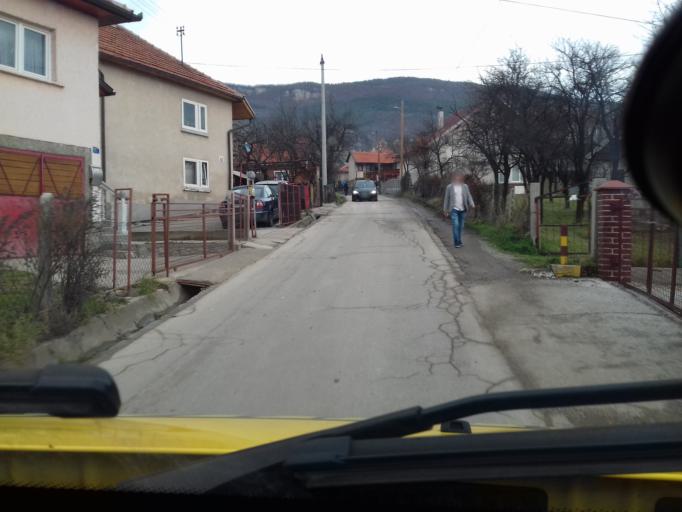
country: BA
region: Federation of Bosnia and Herzegovina
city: Zenica
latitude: 44.1944
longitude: 17.9418
